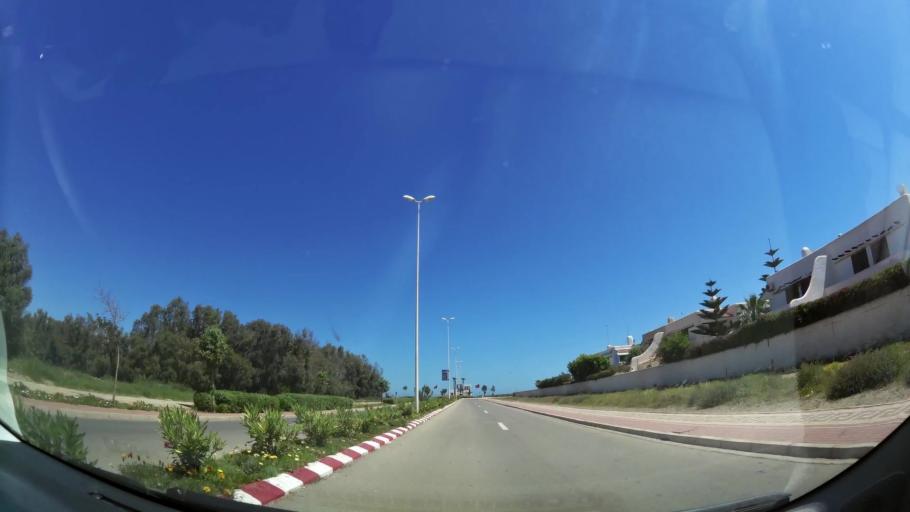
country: MA
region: Oriental
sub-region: Berkane-Taourirt
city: Madagh
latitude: 35.0948
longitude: -2.2650
